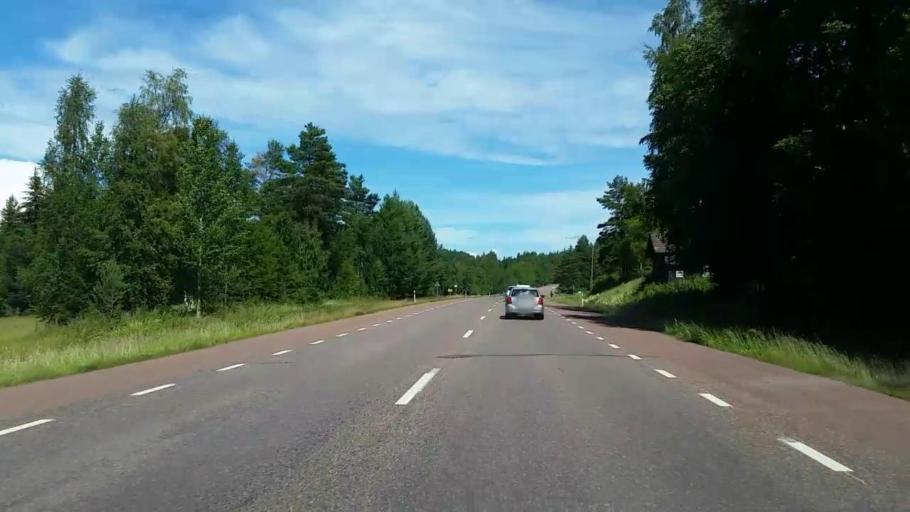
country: SE
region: Dalarna
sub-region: Rattviks Kommun
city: Raettvik
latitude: 60.9200
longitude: 15.2080
